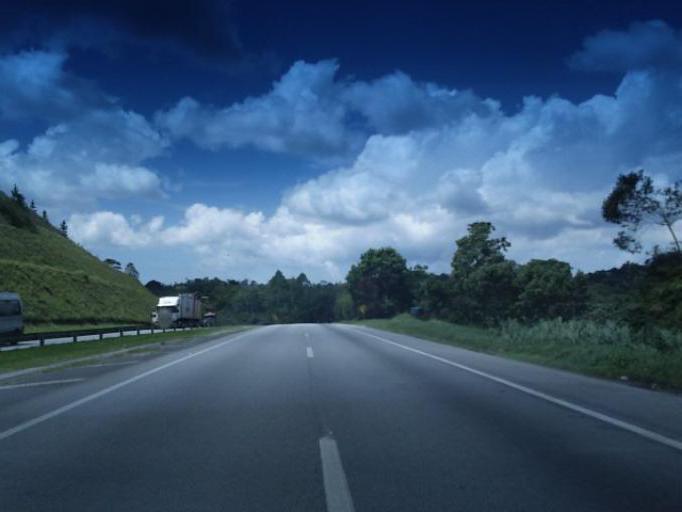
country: BR
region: Sao Paulo
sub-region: Juquitiba
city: Juquitiba
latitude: -23.9850
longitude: -47.1474
